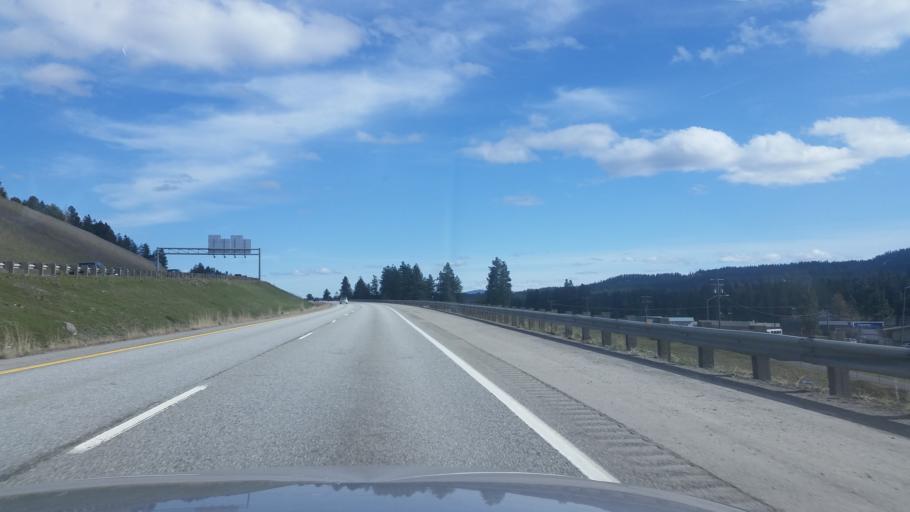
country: US
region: Idaho
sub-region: Kootenai County
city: Post Falls
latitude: 47.7102
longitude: -116.8949
